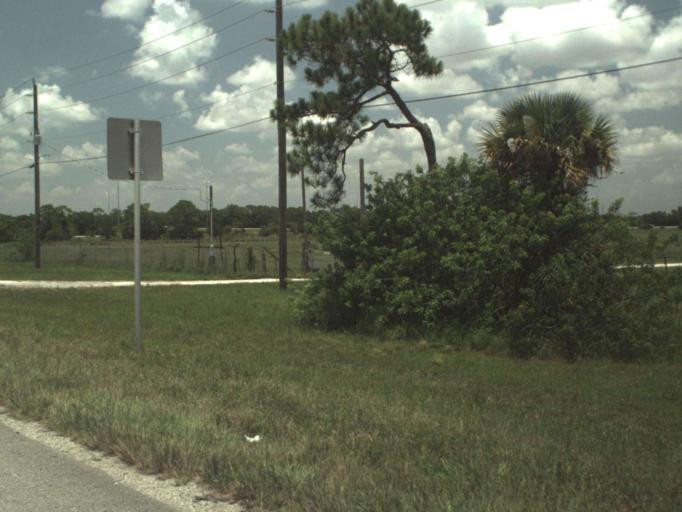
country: US
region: Florida
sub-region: Saint Lucie County
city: Fort Pierce South
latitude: 27.3746
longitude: -80.4028
